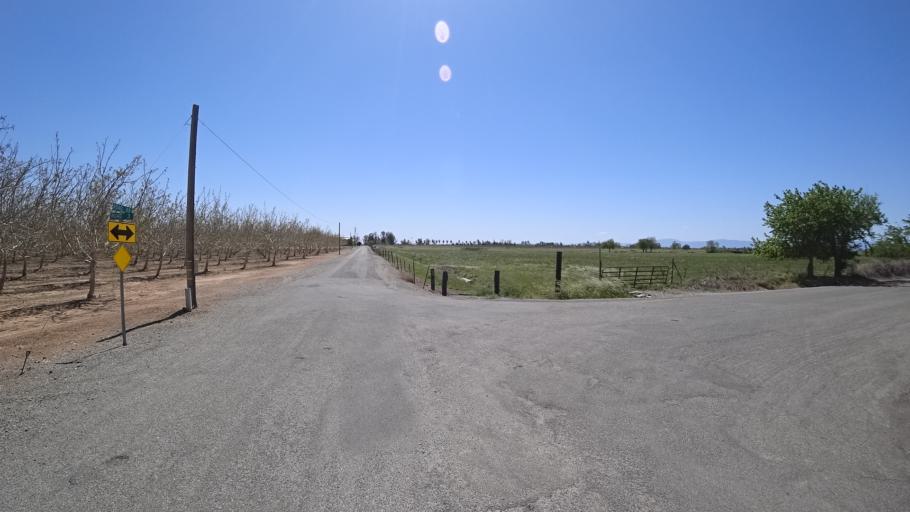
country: US
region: California
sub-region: Glenn County
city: Orland
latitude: 39.7945
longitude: -122.1857
